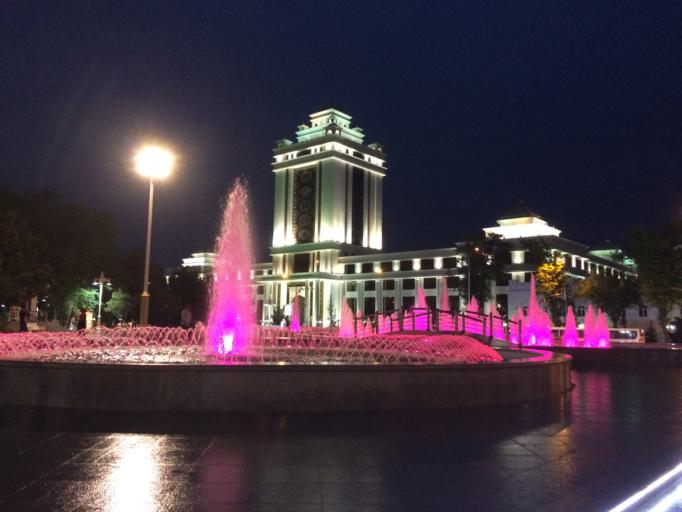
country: TM
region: Ahal
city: Ashgabat
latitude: 37.9393
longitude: 58.3921
